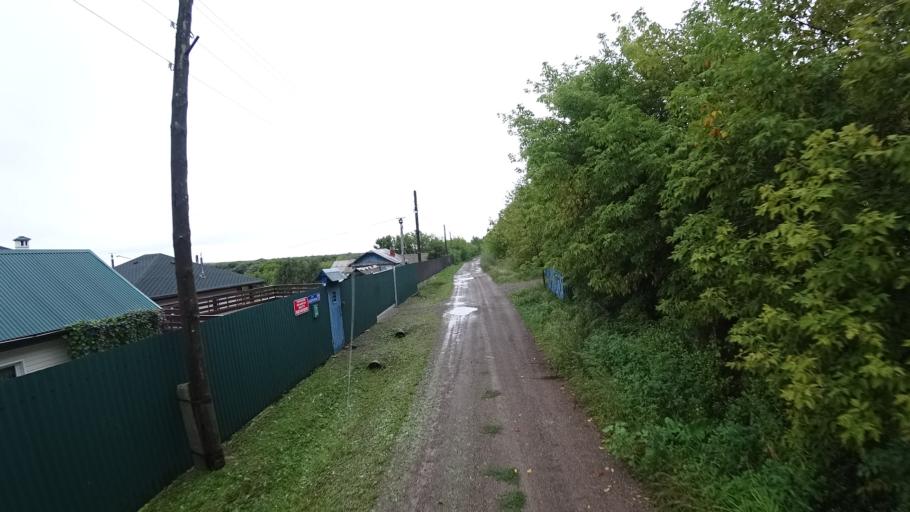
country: RU
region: Primorskiy
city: Monastyrishche
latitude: 44.2645
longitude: 132.4044
